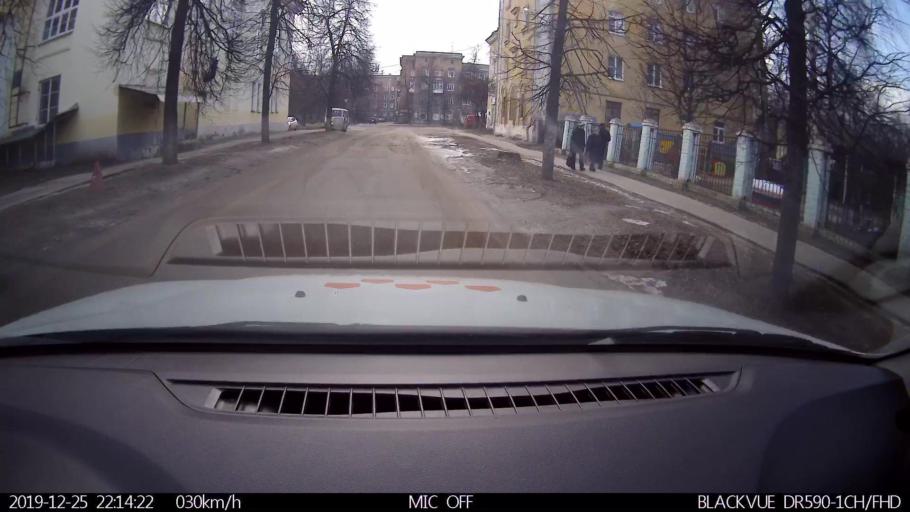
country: RU
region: Nizjnij Novgorod
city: Gorbatovka
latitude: 56.3314
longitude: 43.8457
